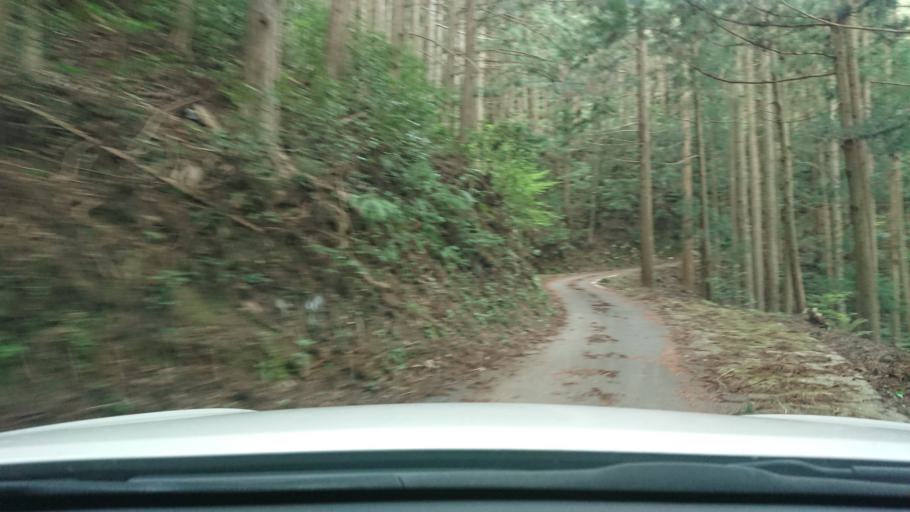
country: JP
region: Tokushima
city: Kamojimacho-jogejima
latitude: 33.8841
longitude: 134.3842
